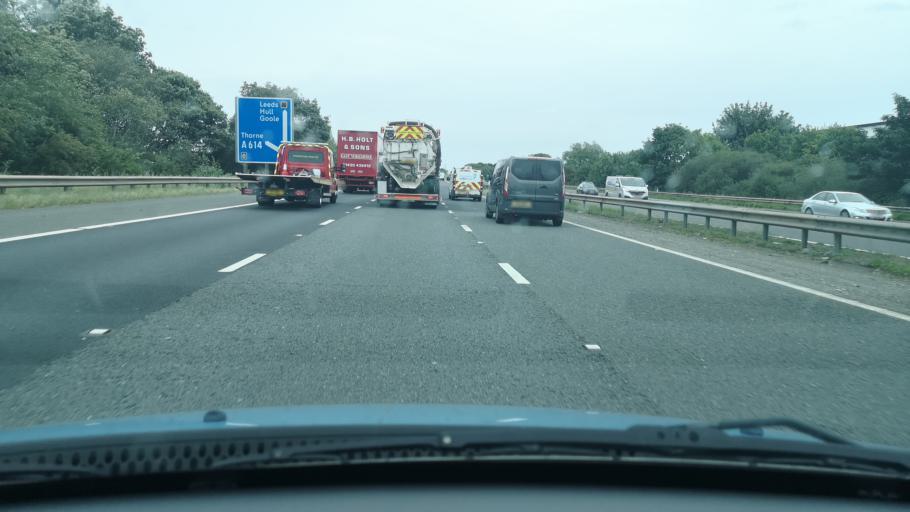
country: GB
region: England
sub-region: Doncaster
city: Hatfield
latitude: 53.6143
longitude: -0.9843
